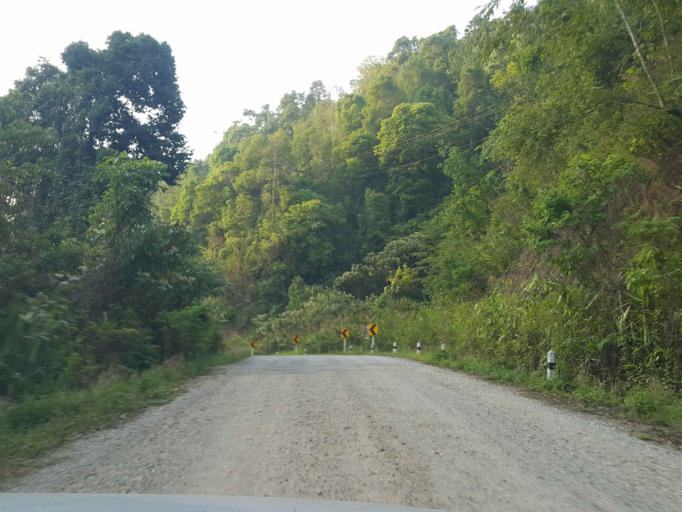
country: TH
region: Chiang Mai
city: Mae On
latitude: 18.9531
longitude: 99.3453
